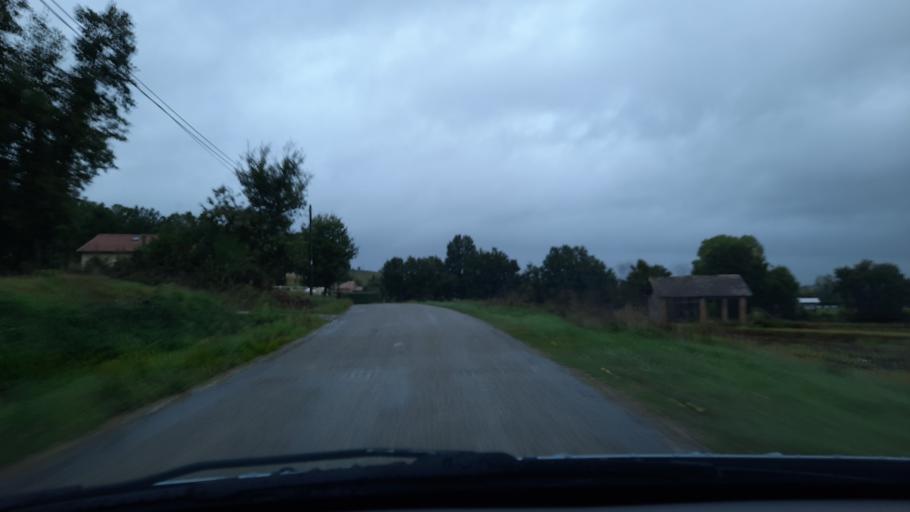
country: FR
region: Midi-Pyrenees
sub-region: Departement du Tarn-et-Garonne
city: Lafrancaise
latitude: 44.1875
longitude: 1.2771
